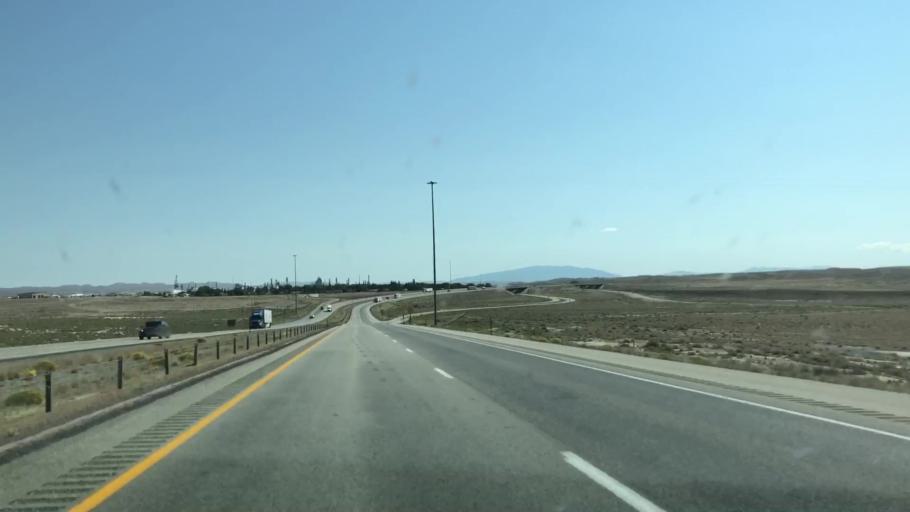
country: US
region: Wyoming
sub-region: Carbon County
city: Rawlins
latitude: 41.7815
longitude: -107.1399
